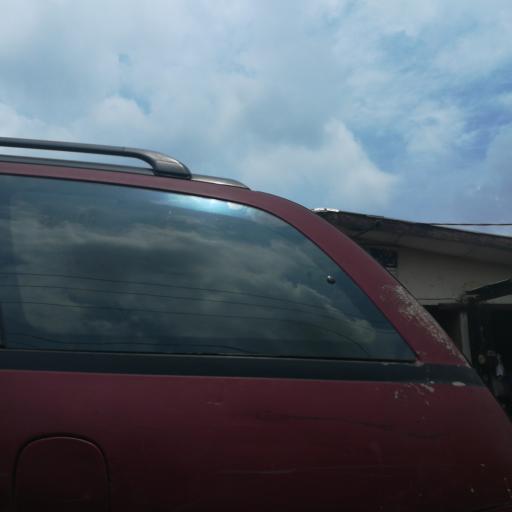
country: NG
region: Lagos
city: Ojota
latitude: 6.5829
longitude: 3.3824
